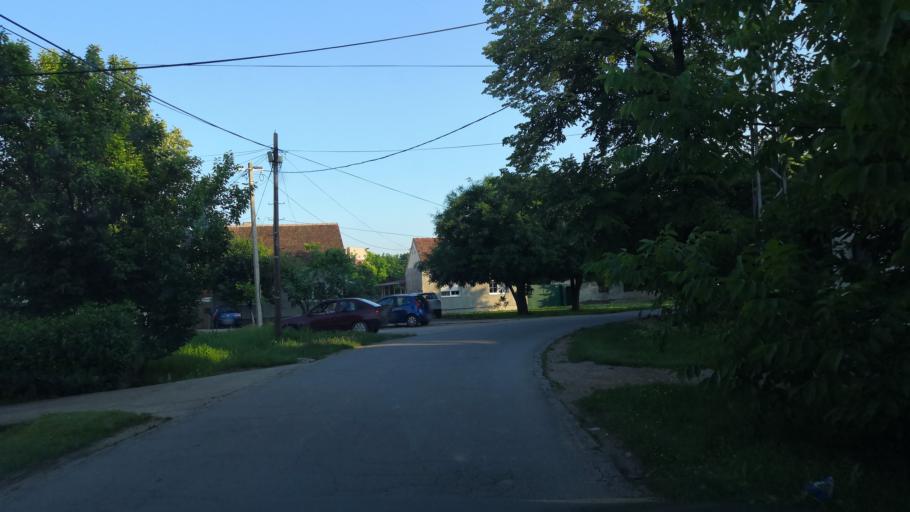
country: RS
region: Autonomna Pokrajina Vojvodina
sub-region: Sremski Okrug
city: Stara Pazova
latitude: 44.9888
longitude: 20.1625
